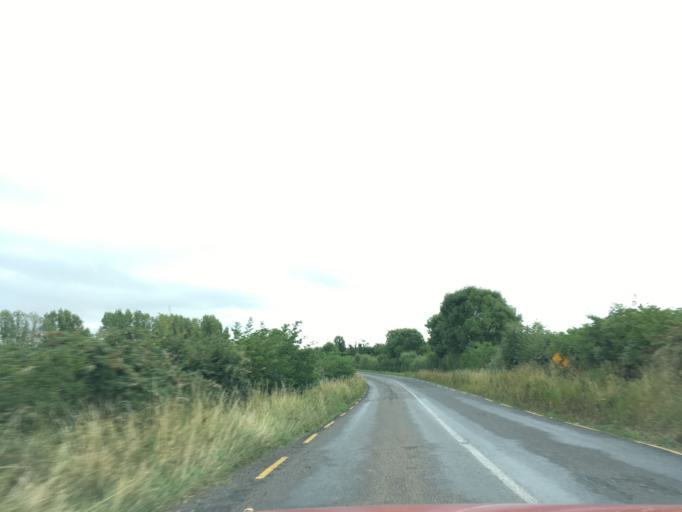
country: IE
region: Munster
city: Cashel
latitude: 52.4501
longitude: -7.8116
